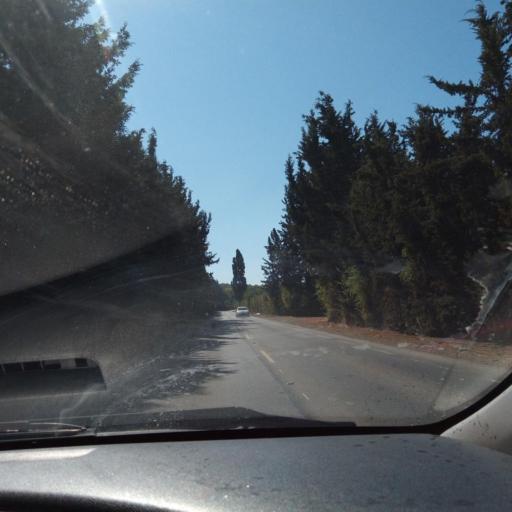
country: CY
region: Larnaka
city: Kolossi
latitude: 34.6324
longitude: 32.9479
